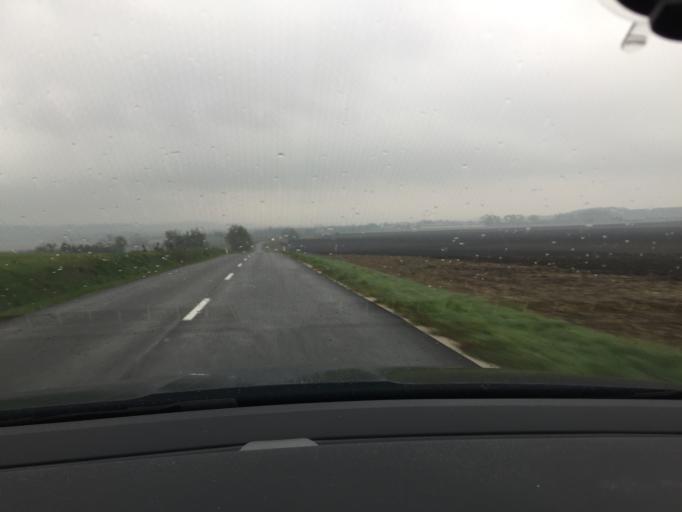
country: SK
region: Nitriansky
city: Zeliezovce
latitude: 48.0415
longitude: 18.8008
